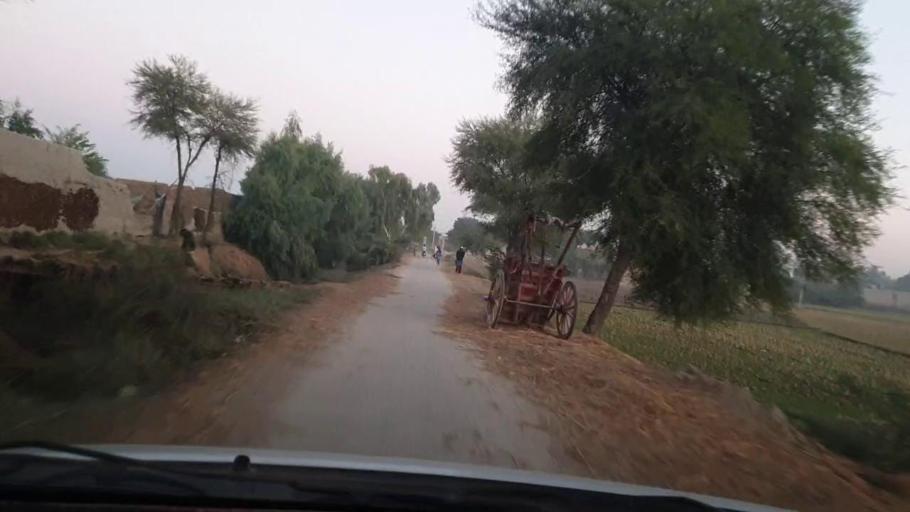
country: PK
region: Sindh
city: Khairpur Nathan Shah
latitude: 27.1459
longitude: 67.7046
